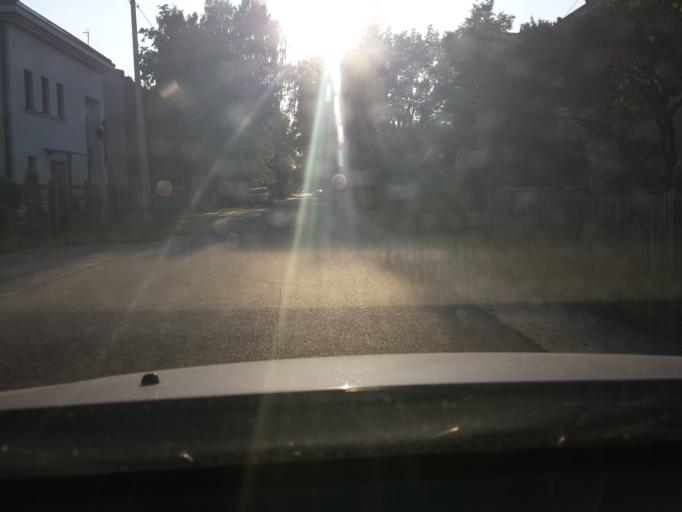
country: LV
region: Riga
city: Jaunciems
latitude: 56.9712
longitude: 24.1874
